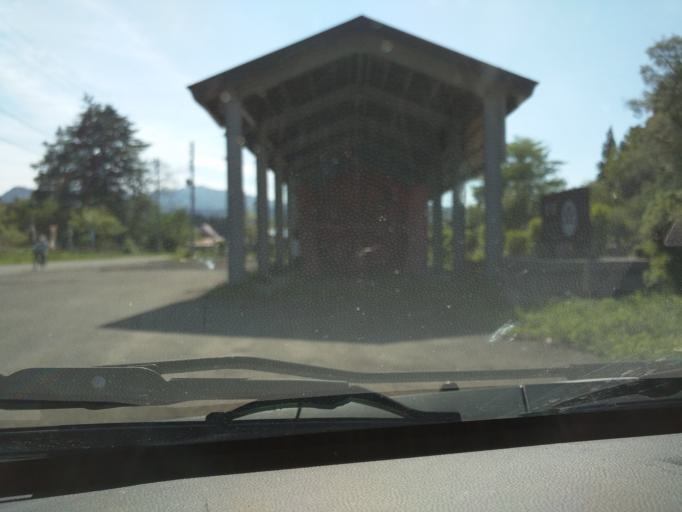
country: JP
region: Fukushima
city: Kitakata
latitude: 37.5760
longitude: 139.6409
